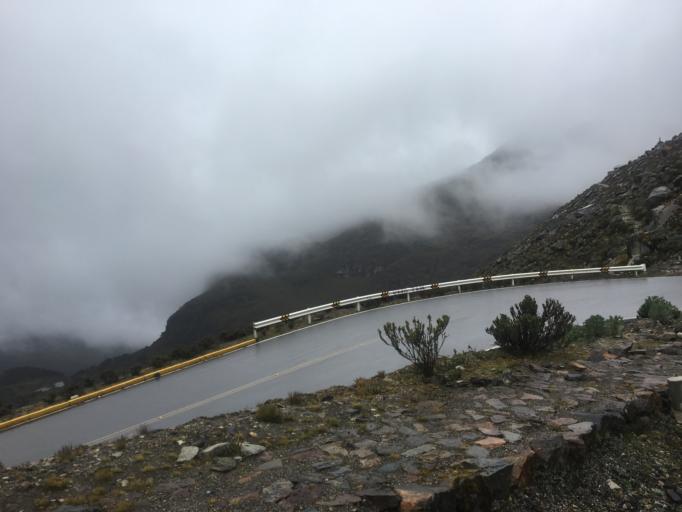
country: PE
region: Ancash
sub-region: Provincia de Yungay
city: Yanama
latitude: -9.1401
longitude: -77.5042
